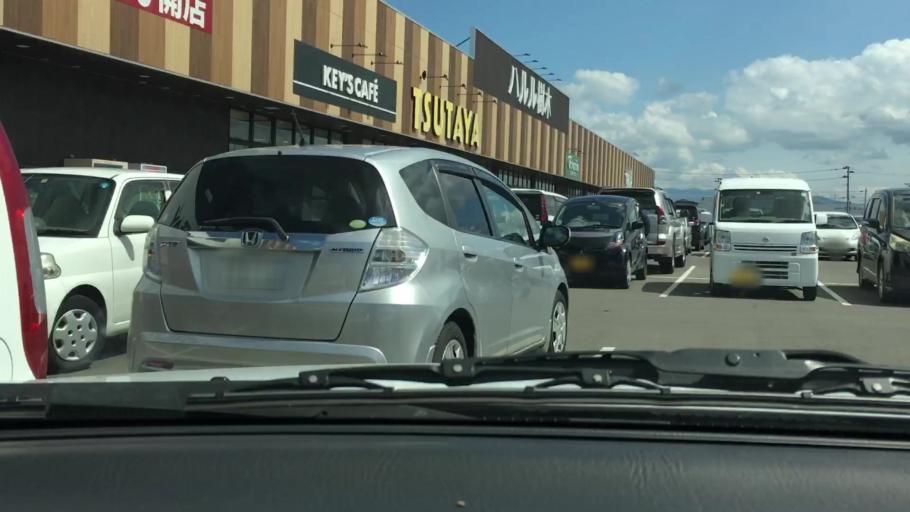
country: JP
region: Aomori
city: Hirosaki
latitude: 40.5875
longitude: 140.4589
